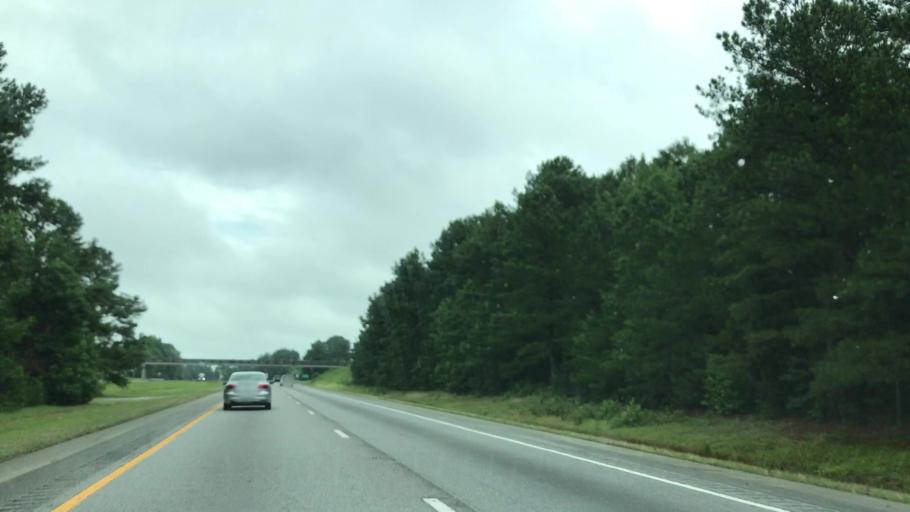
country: US
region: North Carolina
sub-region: Northampton County
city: Gaston
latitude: 36.4835
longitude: -77.6036
